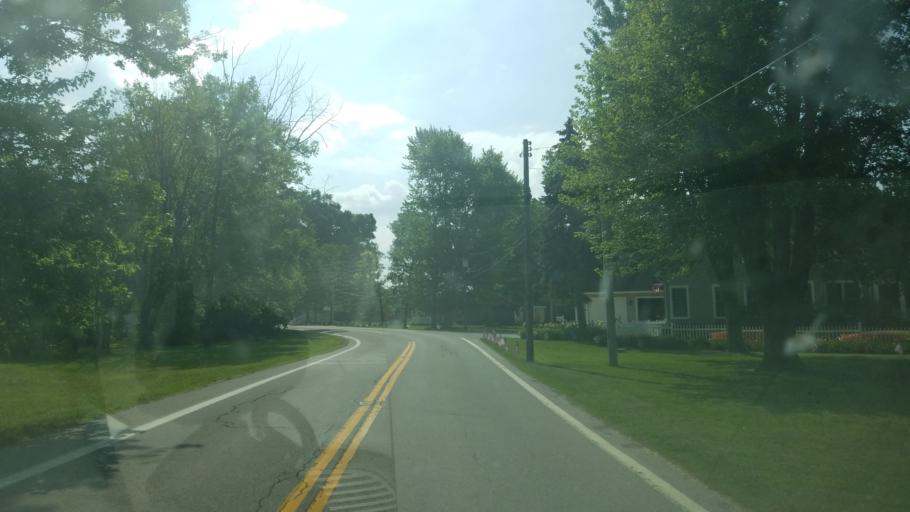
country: US
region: Ohio
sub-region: Logan County
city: Russells Point
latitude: 40.5050
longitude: -83.8526
